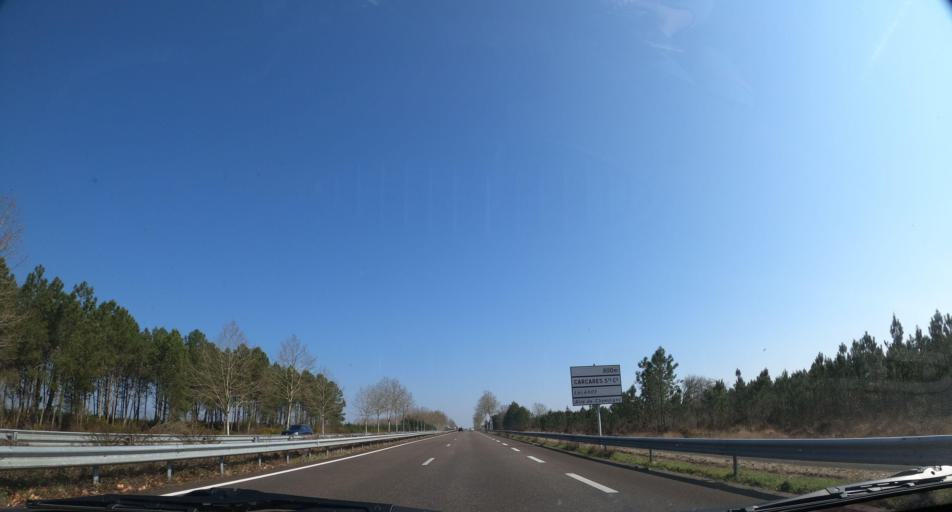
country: FR
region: Aquitaine
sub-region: Departement des Landes
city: Tartas
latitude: 43.8384
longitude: -0.7722
